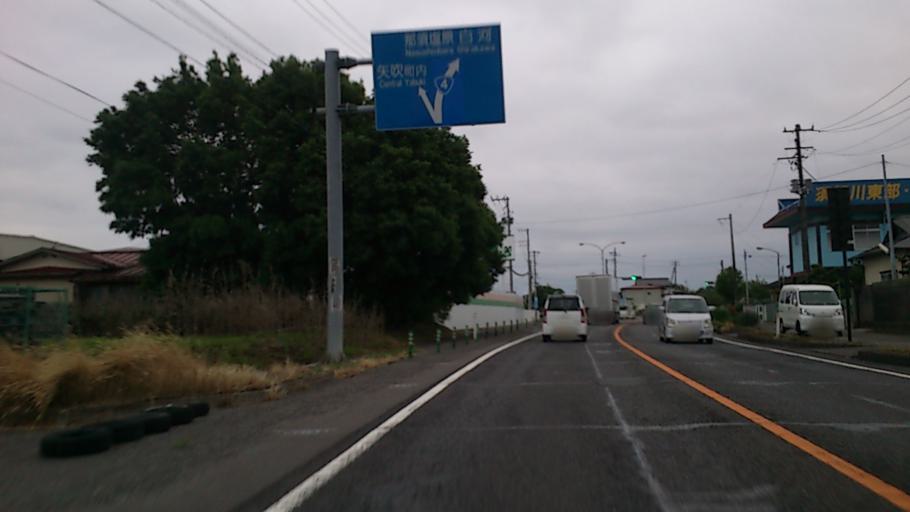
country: JP
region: Fukushima
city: Sukagawa
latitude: 37.2169
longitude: 140.3281
